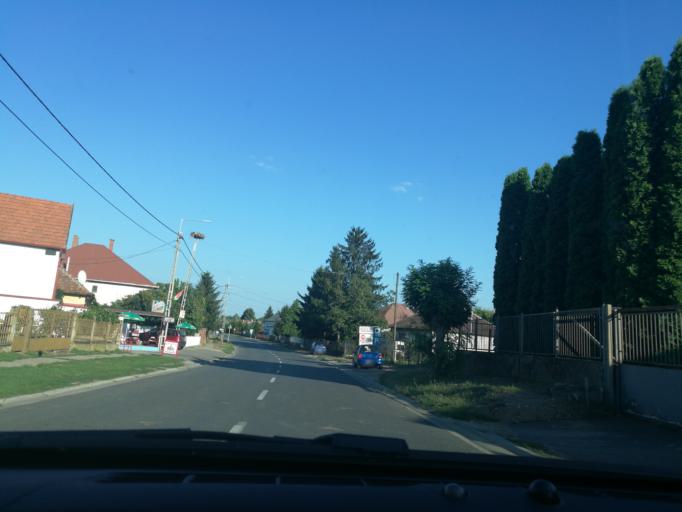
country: HU
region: Szabolcs-Szatmar-Bereg
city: Tiszabercel
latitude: 48.1588
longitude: 21.5997
